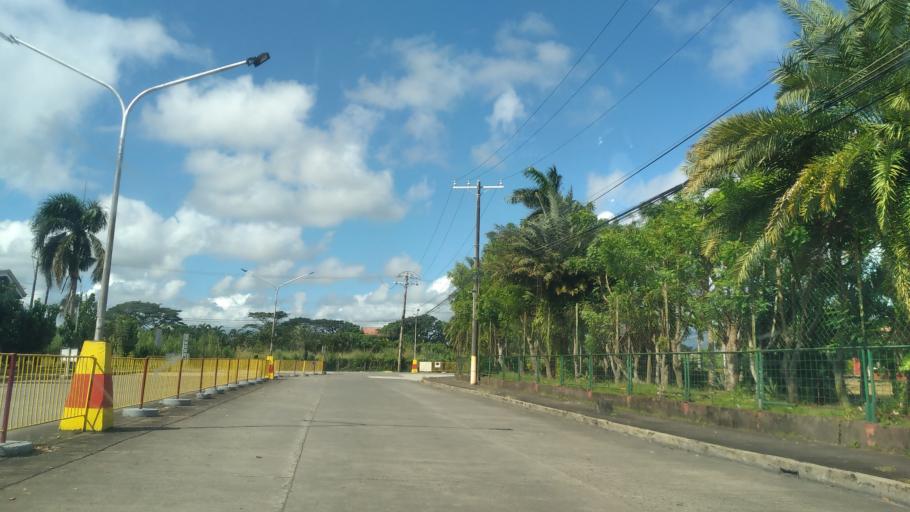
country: PH
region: Calabarzon
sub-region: Province of Quezon
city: Lucena
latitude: 13.9592
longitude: 121.6170
